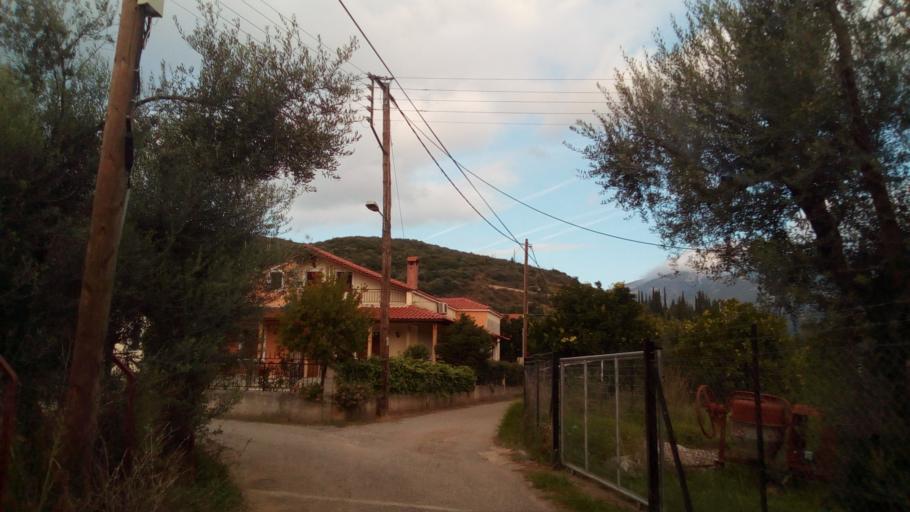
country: GR
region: West Greece
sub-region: Nomos Aitolias kai Akarnanias
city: Nafpaktos
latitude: 38.3830
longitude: 21.7974
